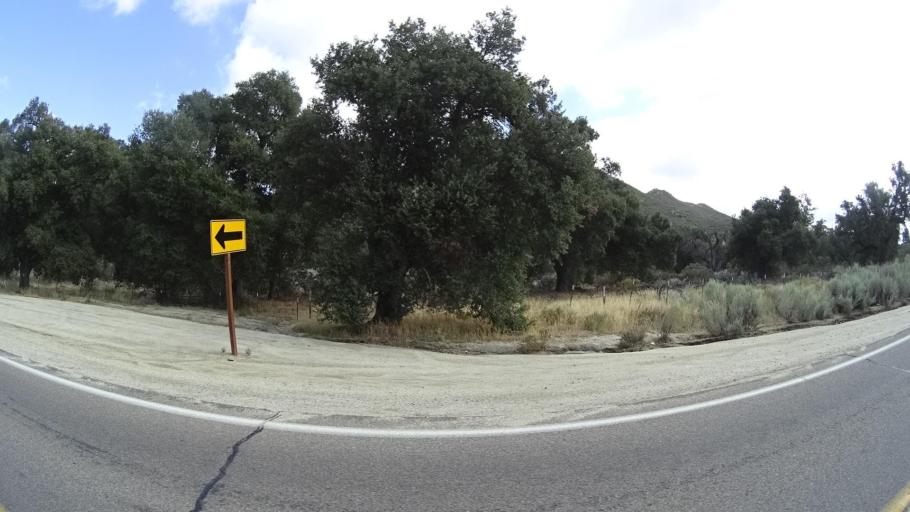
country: US
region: California
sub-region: San Diego County
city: Campo
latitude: 32.6991
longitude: -116.4890
